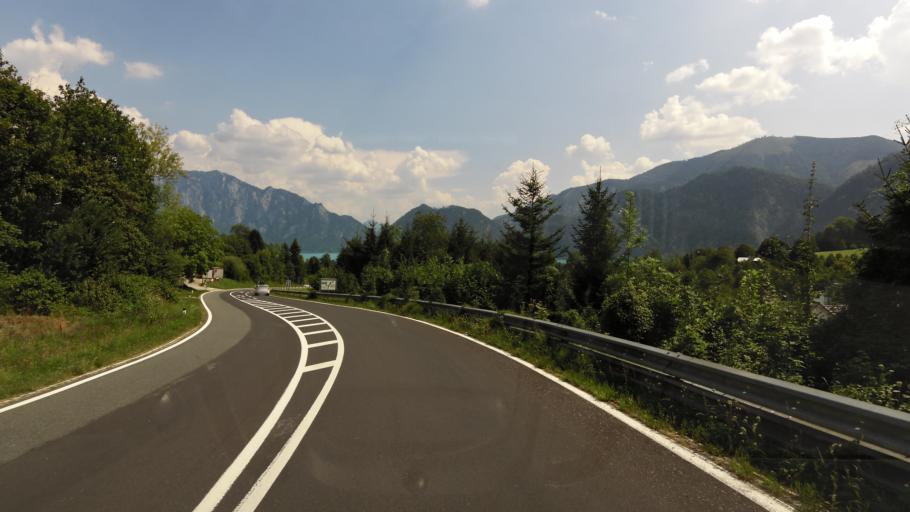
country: AT
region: Upper Austria
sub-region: Politischer Bezirk Gmunden
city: Sankt Wolfgang im Salzkammergut
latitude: 47.8028
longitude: 13.4777
